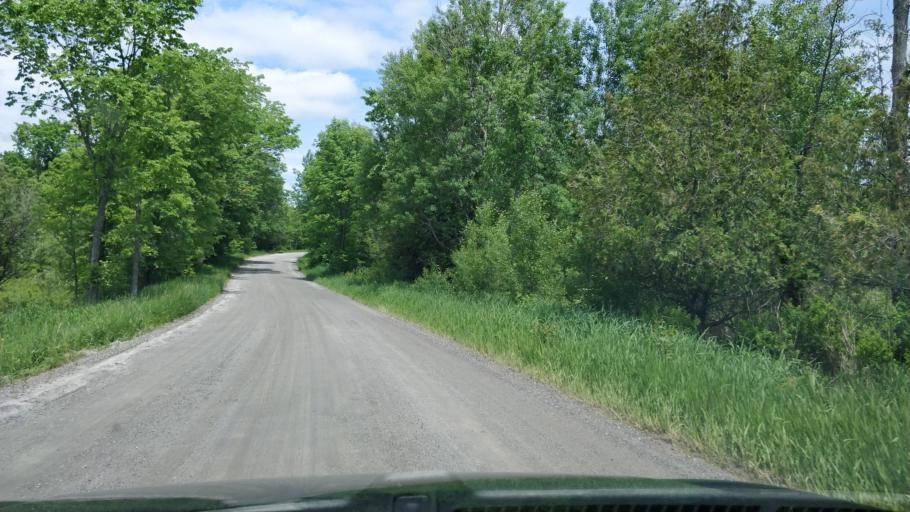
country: CA
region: Ontario
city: Perth
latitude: 44.7292
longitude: -76.5076
